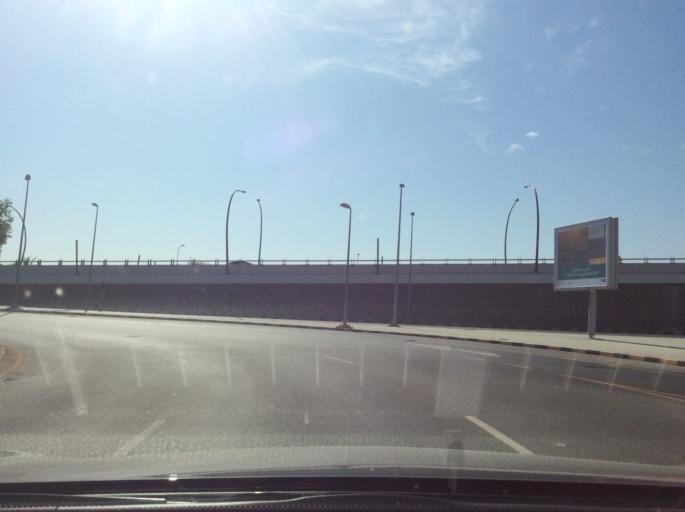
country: OM
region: Muhafazat Masqat
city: Bawshar
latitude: 23.5989
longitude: 58.2923
